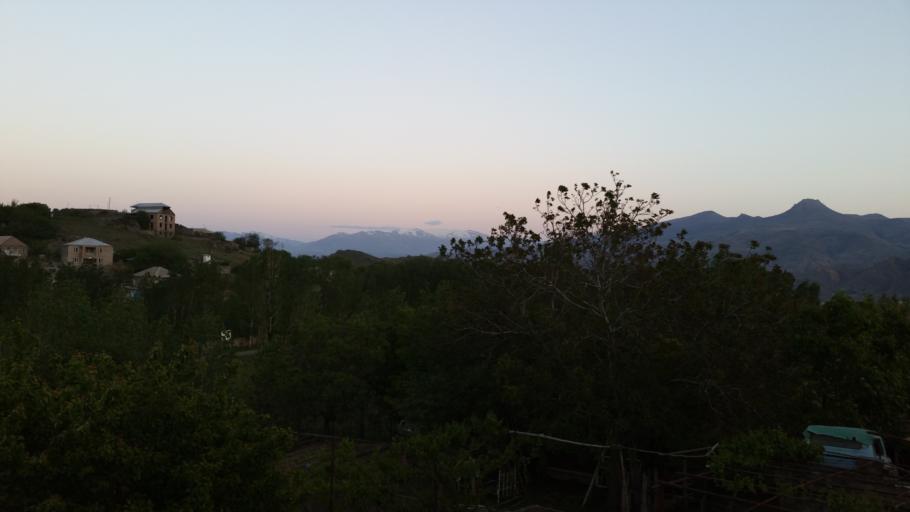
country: AM
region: Vayots' Dzori Marz
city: Yeghegnadzor
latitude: 39.7693
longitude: 45.3294
